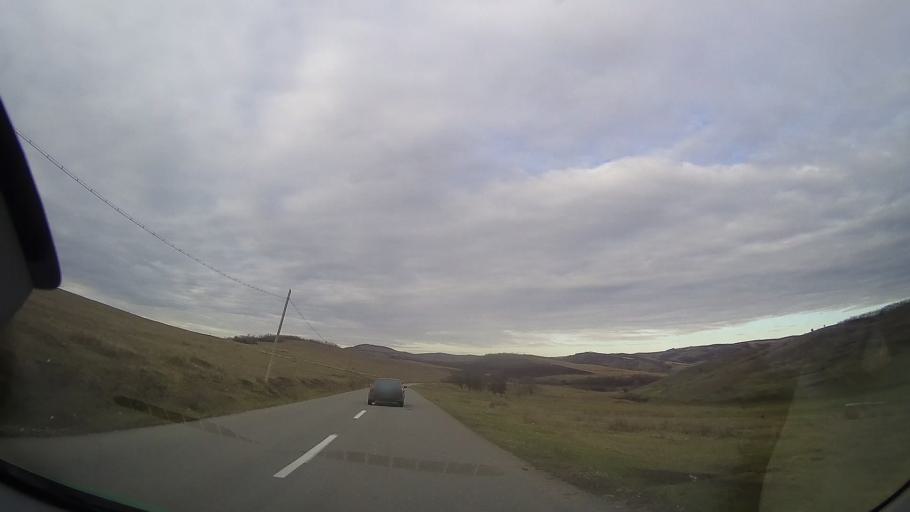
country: RO
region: Bistrita-Nasaud
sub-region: Comuna Milas
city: Milas
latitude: 46.8260
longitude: 24.4532
